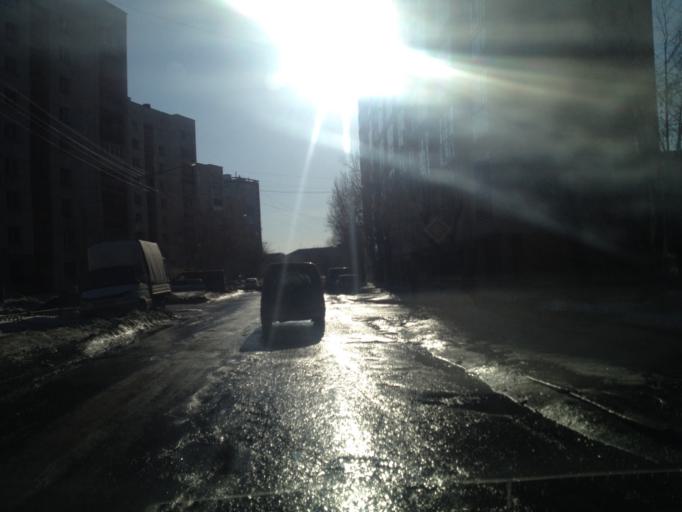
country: RU
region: Sverdlovsk
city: Yekaterinburg
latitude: 56.9070
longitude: 60.6185
